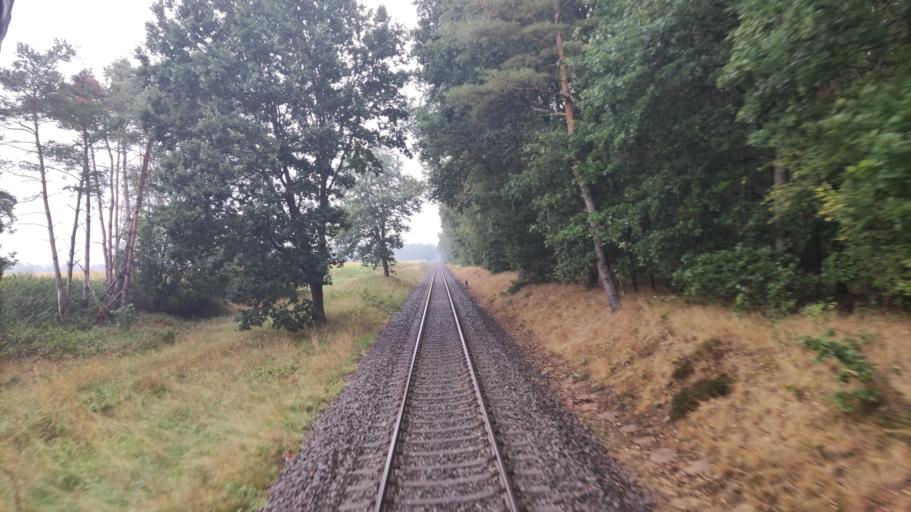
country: DE
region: Lower Saxony
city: Bispingen
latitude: 53.0410
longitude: 9.9390
